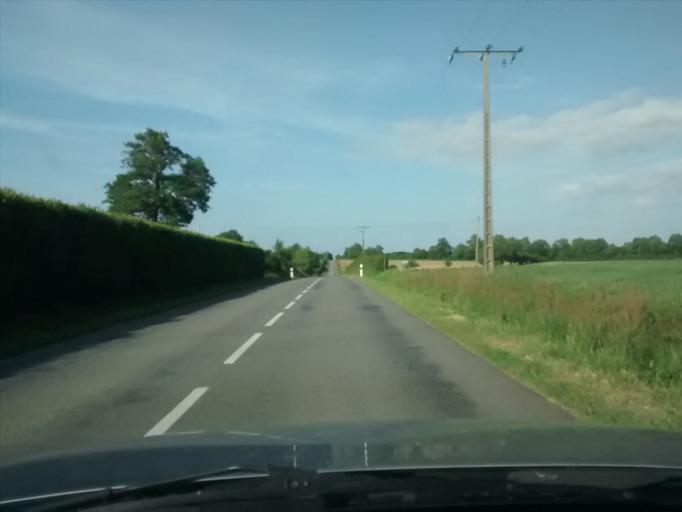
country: FR
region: Pays de la Loire
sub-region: Departement de la Mayenne
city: Entrammes
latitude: 47.9293
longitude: -0.6632
